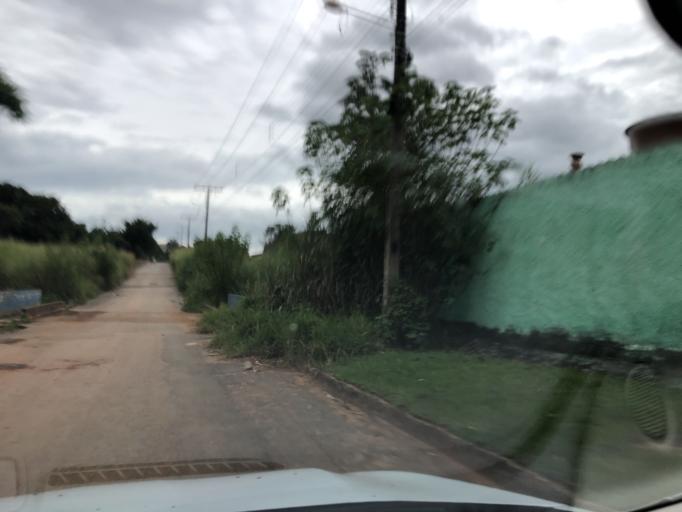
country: BR
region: Goias
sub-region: Luziania
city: Luziania
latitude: -16.1597
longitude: -47.9487
